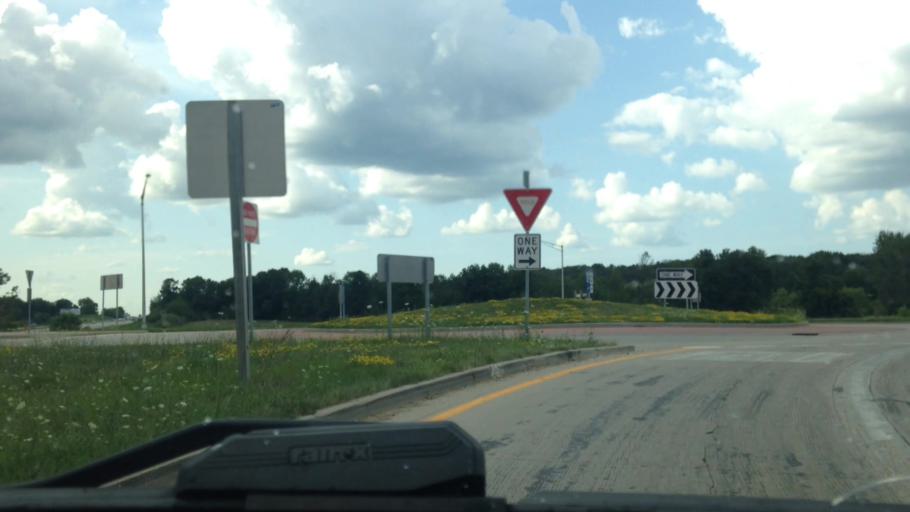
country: US
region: Wisconsin
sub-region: Washington County
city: Richfield
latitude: 43.2821
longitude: -88.1933
